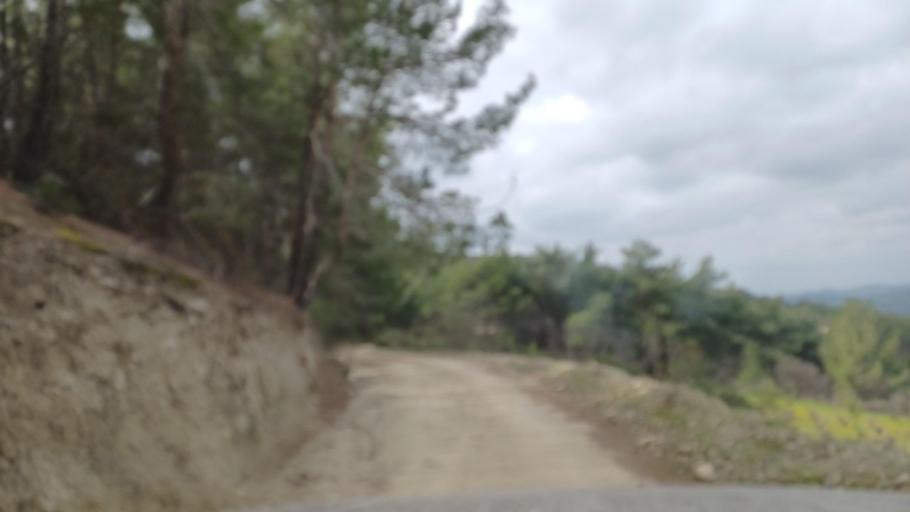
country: CY
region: Limassol
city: Pachna
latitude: 34.7741
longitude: 32.6954
